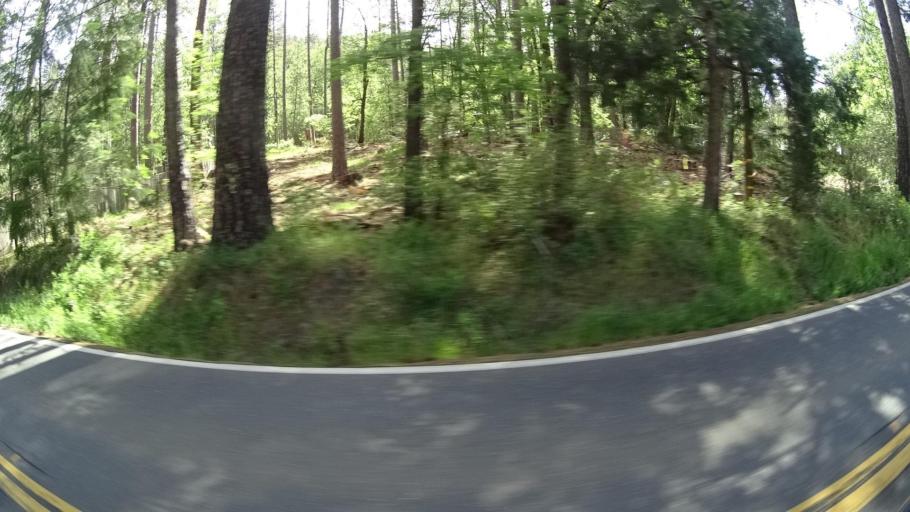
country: US
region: California
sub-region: Lake County
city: Cobb
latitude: 38.8641
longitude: -122.7186
